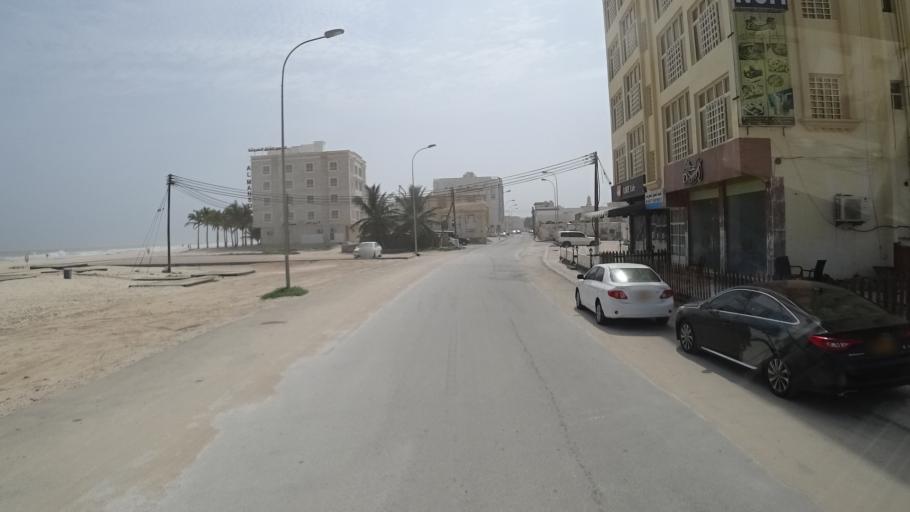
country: OM
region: Zufar
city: Salalah
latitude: 17.0100
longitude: 54.1639
